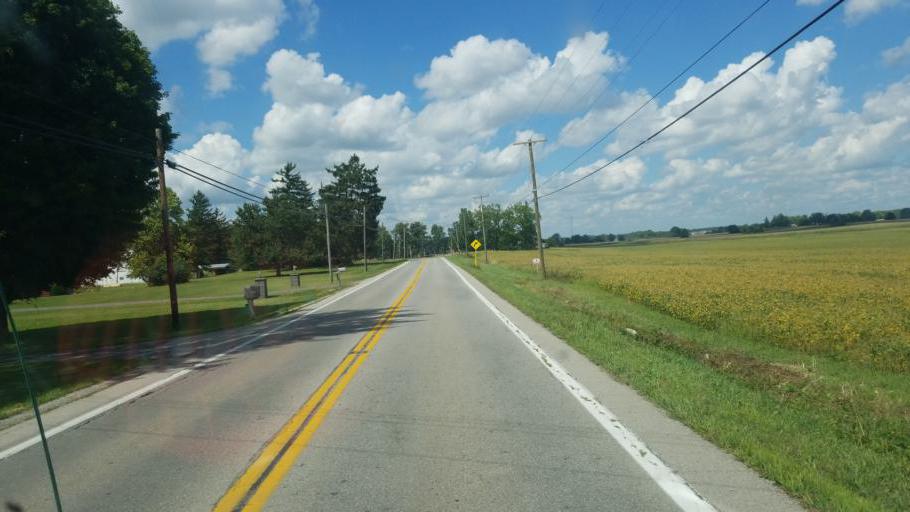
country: US
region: Ohio
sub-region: Marion County
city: Marion
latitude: 40.5361
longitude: -83.1075
